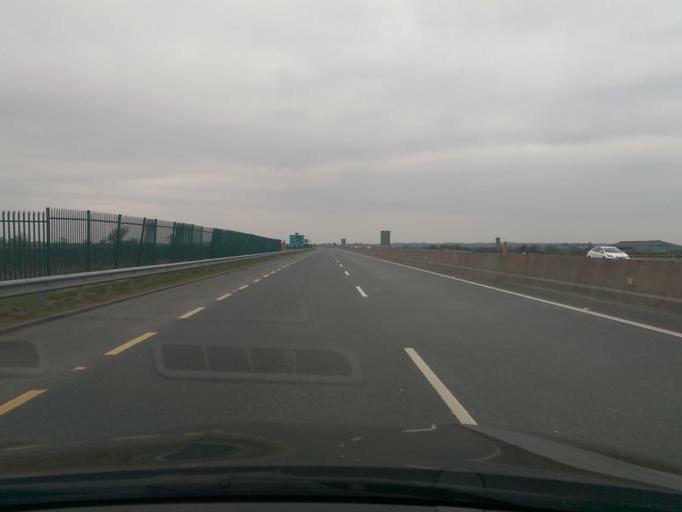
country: IE
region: Connaught
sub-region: County Galway
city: Oranmore
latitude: 53.2950
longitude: -8.9353
